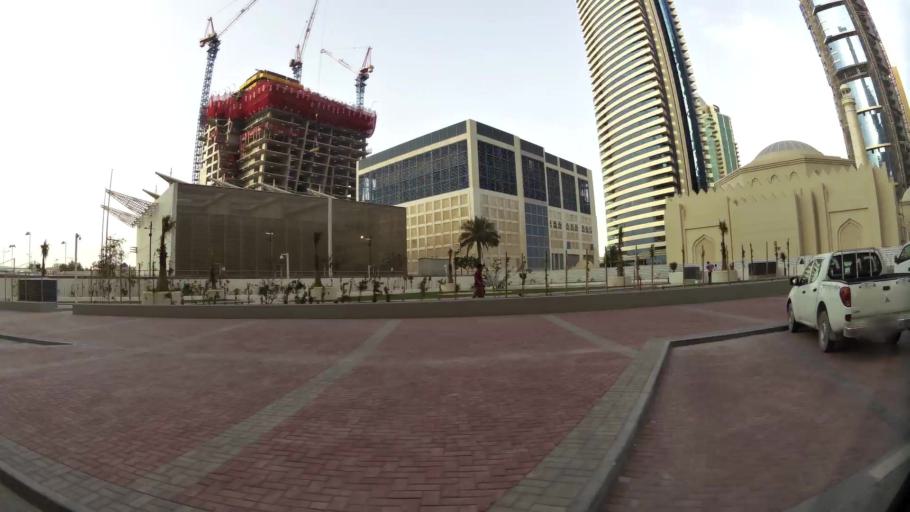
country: QA
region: Baladiyat ad Dawhah
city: Doha
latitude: 25.3289
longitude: 51.5320
